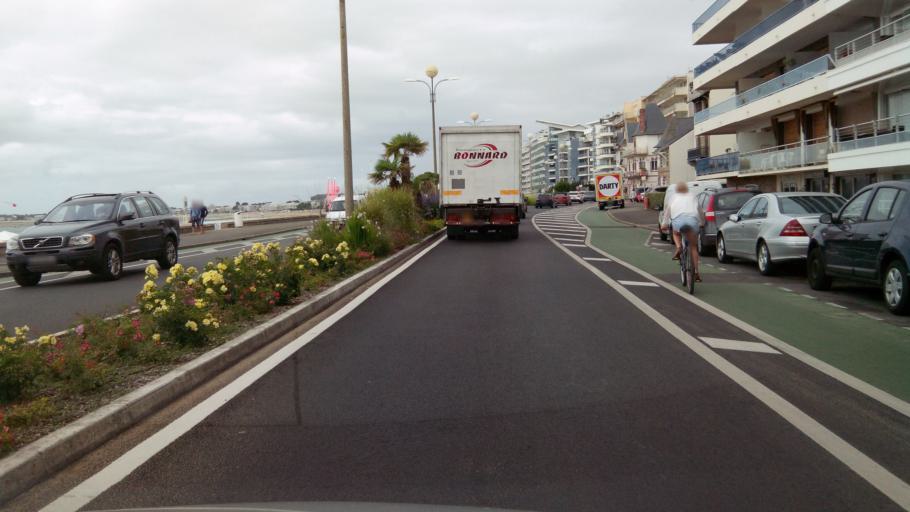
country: FR
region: Pays de la Loire
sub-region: Departement de la Loire-Atlantique
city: La Baule-Escoublac
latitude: 47.2813
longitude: -2.3880
